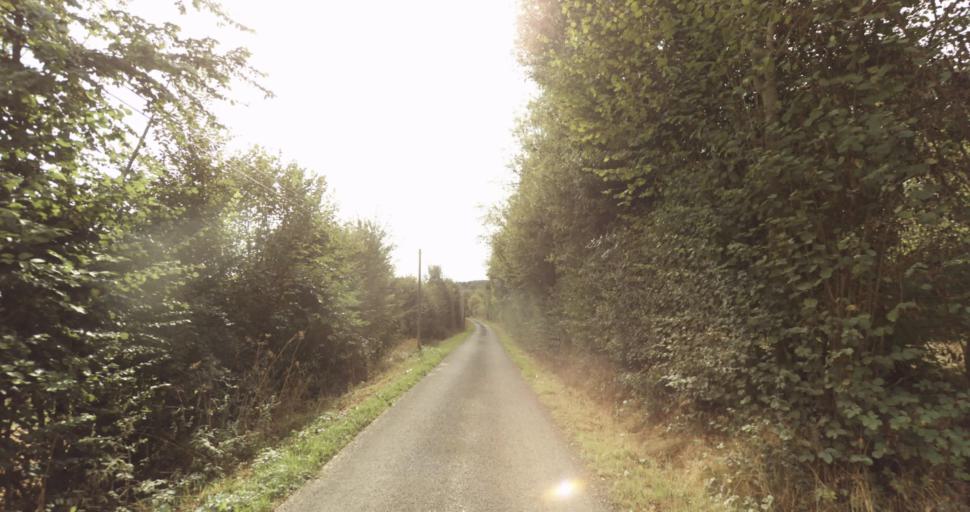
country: FR
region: Lower Normandy
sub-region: Departement de l'Orne
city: Gace
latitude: 48.8475
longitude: 0.2856
